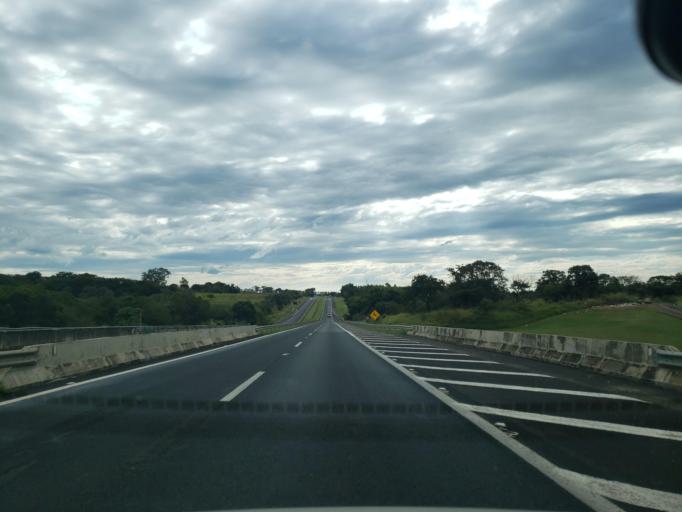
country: BR
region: Sao Paulo
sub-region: Bauru
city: Bauru
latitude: -22.2062
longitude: -49.1827
